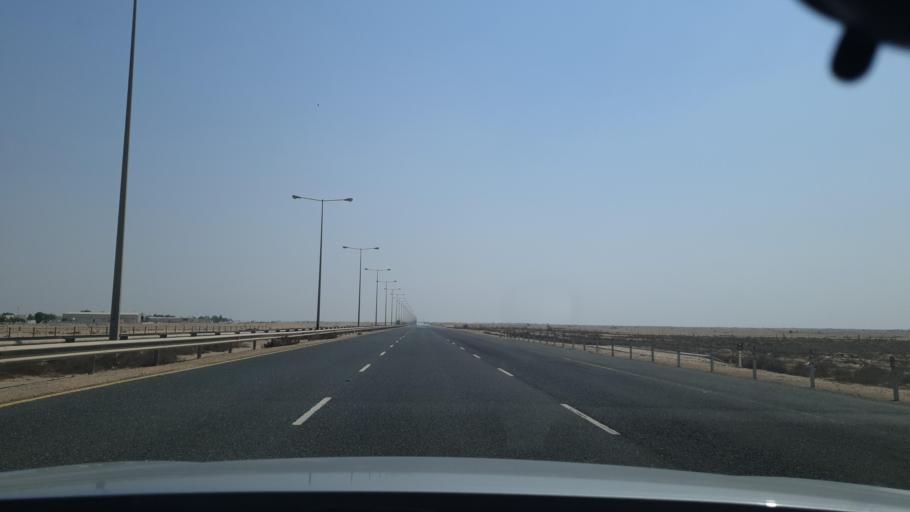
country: QA
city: Al Ghuwayriyah
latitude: 25.8172
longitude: 51.3685
